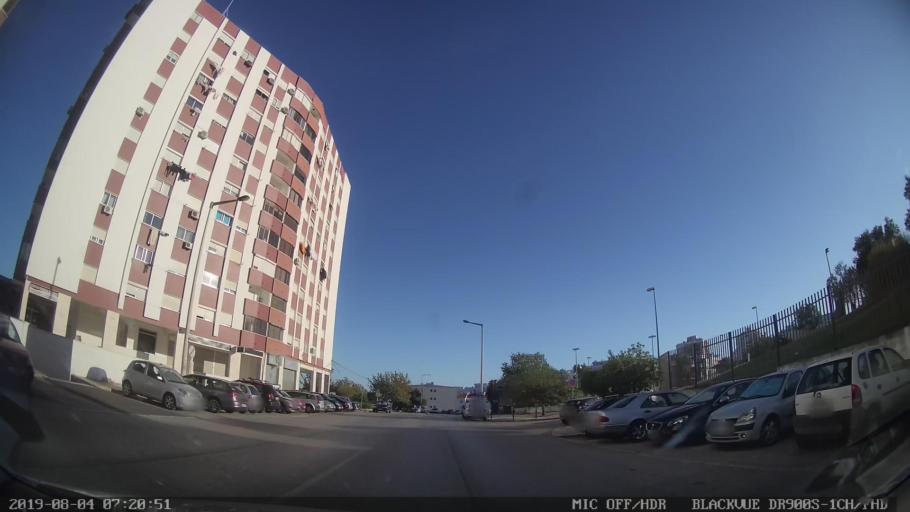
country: PT
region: Lisbon
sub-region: Vila Franca de Xira
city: Povoa de Santa Iria
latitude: 38.8613
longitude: -9.0682
